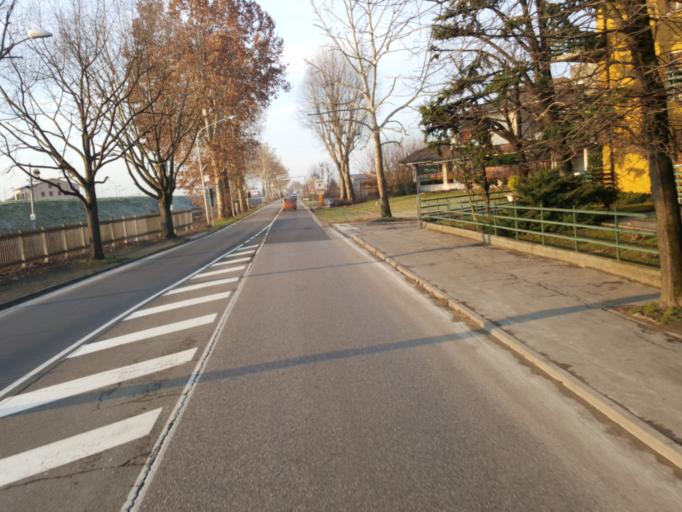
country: IT
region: Emilia-Romagna
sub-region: Provincia di Parma
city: Sorbolo
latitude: 44.8426
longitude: 10.4419
